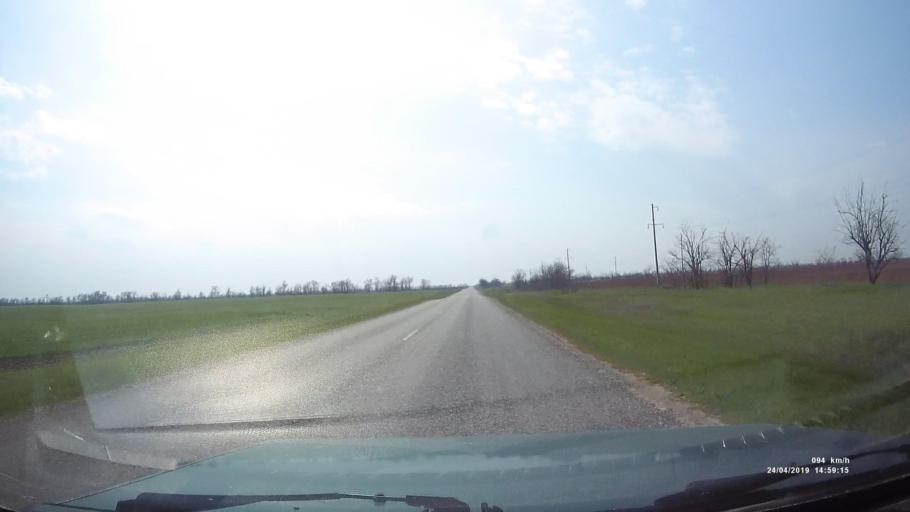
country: RU
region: Rostov
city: Remontnoye
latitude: 46.5662
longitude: 43.5812
